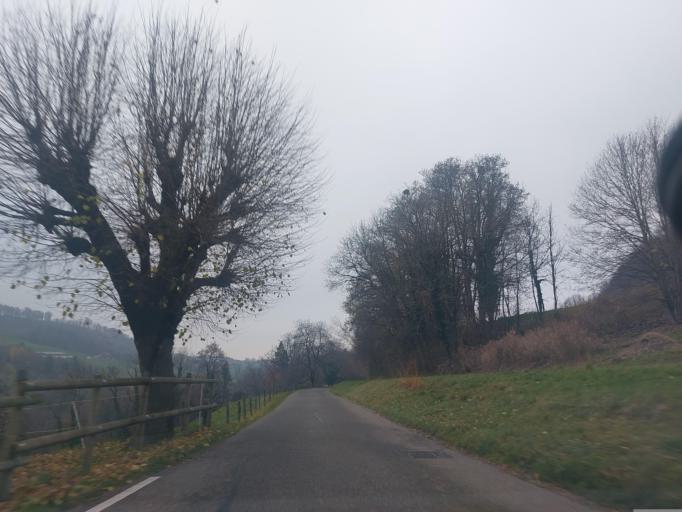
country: CH
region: Fribourg
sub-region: Veveyse District
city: Attalens
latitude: 46.4985
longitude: 6.8802
